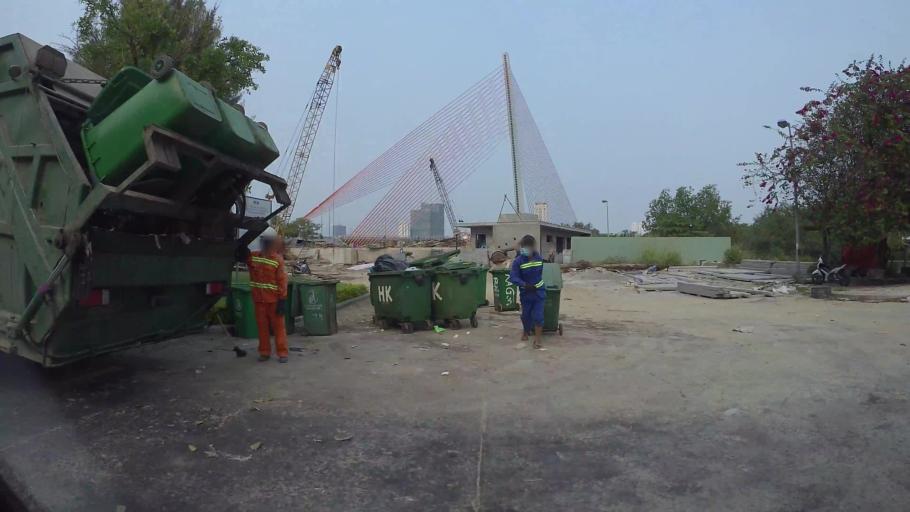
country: VN
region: Da Nang
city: Son Tra
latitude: 16.0489
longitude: 108.2260
